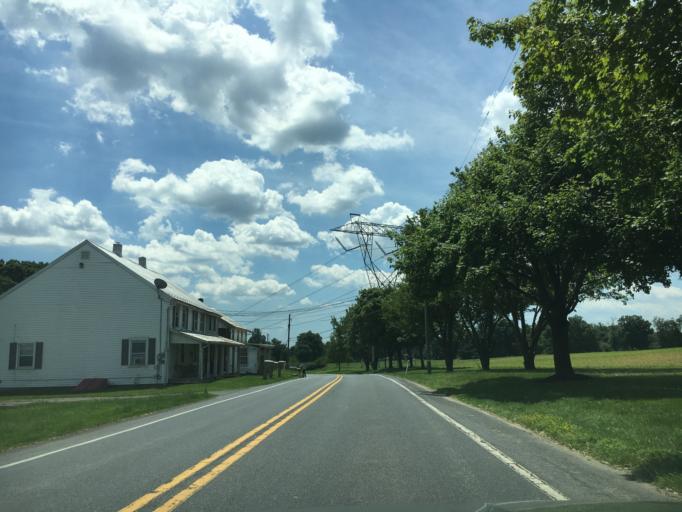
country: US
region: Pennsylvania
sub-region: Lehigh County
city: Schnecksville
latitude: 40.6495
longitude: -75.5776
